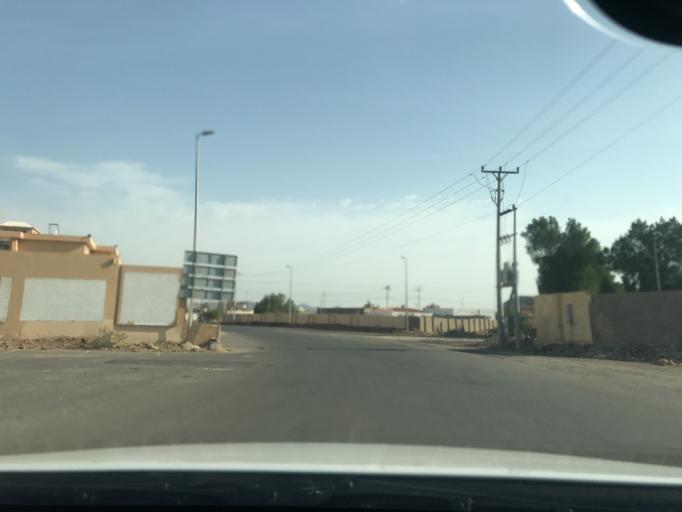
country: SA
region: Makkah
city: Al Jumum
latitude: 21.4520
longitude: 39.5392
